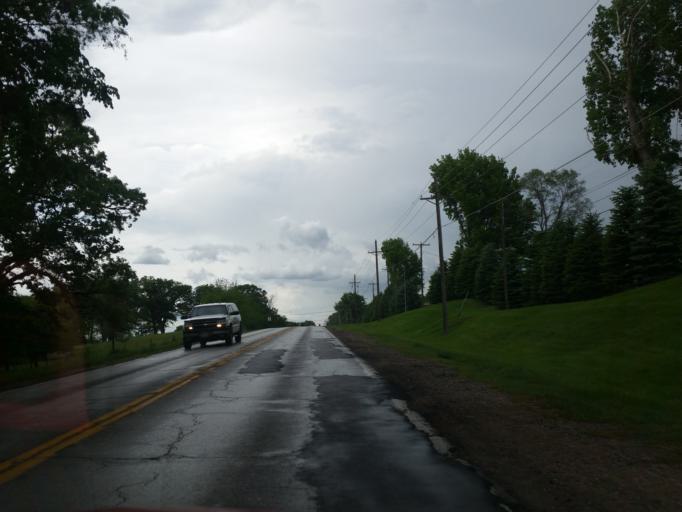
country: US
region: Nebraska
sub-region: Sarpy County
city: Offutt Air Force Base
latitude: 41.1192
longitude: -95.9665
